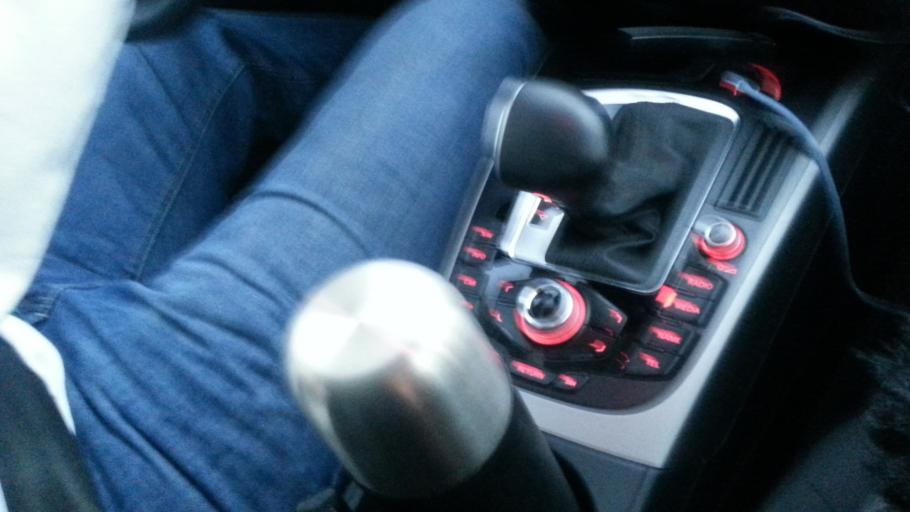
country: FI
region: Lapland
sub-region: Tunturi-Lappi
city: Kittilae
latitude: 67.2249
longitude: 24.9233
